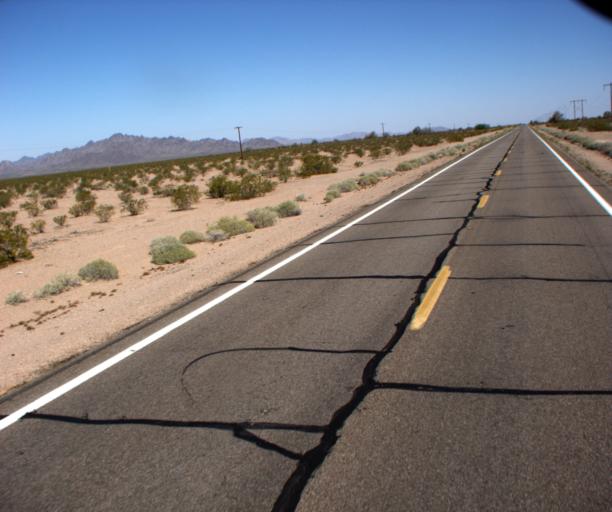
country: US
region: Arizona
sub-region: La Paz County
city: Quartzsite
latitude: 33.4334
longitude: -114.2170
